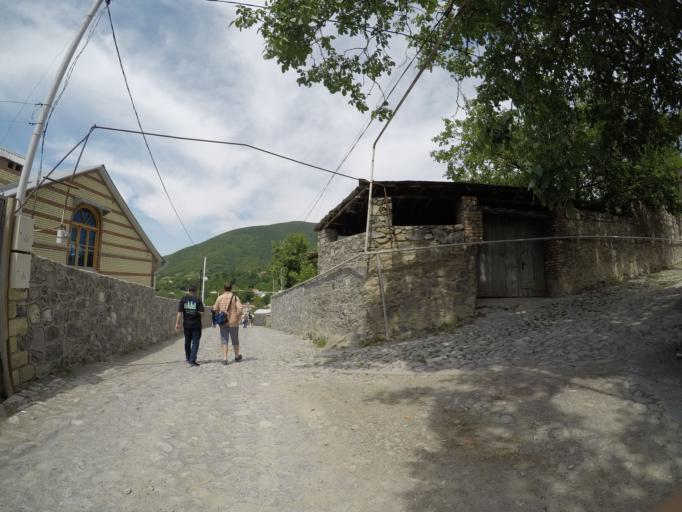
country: AZ
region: Shaki City
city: Sheki
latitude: 41.2471
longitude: 47.1898
